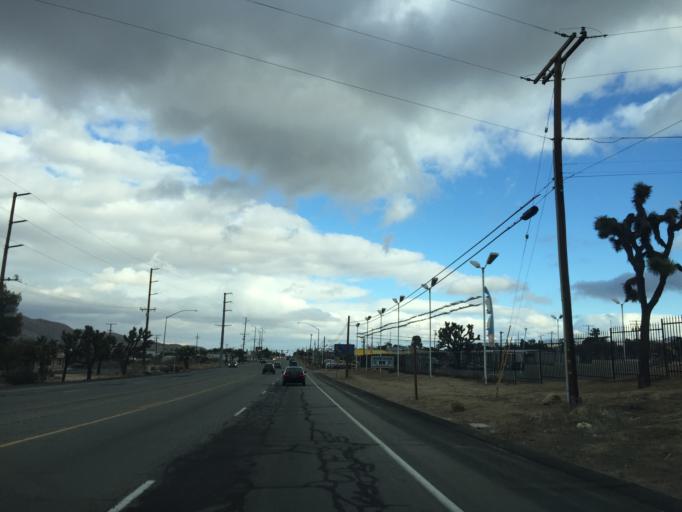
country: US
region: California
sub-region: San Bernardino County
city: Yucca Valley
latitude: 34.1151
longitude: -116.4624
